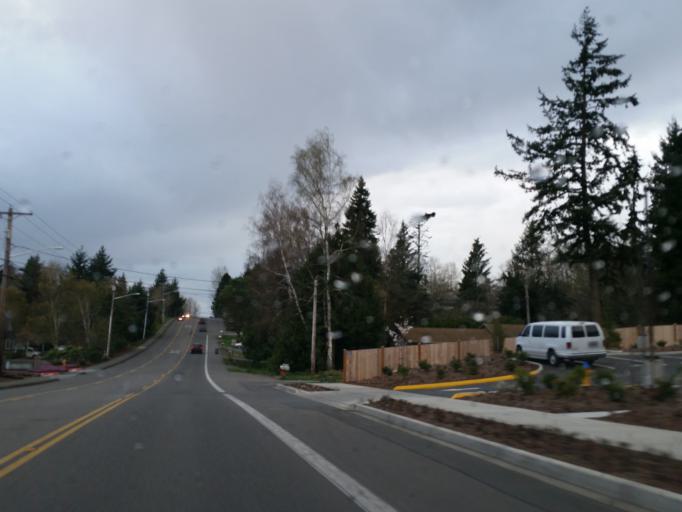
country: US
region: Washington
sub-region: Snohomish County
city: Alderwood Manor
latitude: 47.8137
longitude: -122.2797
